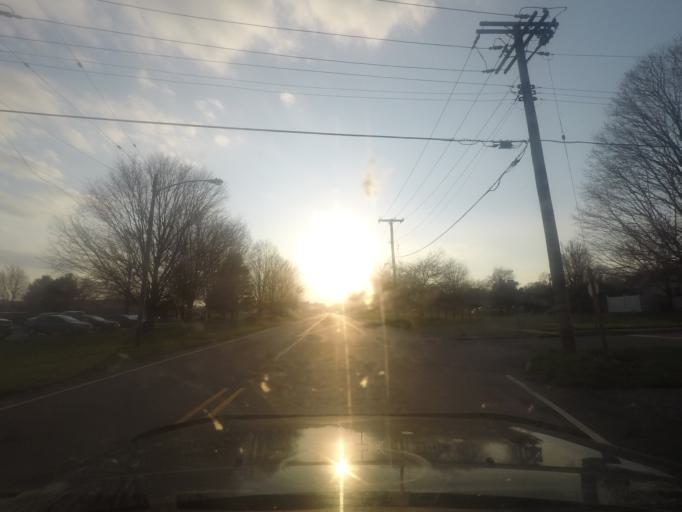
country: US
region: Indiana
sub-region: LaPorte County
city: LaPorte
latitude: 41.5914
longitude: -86.7146
